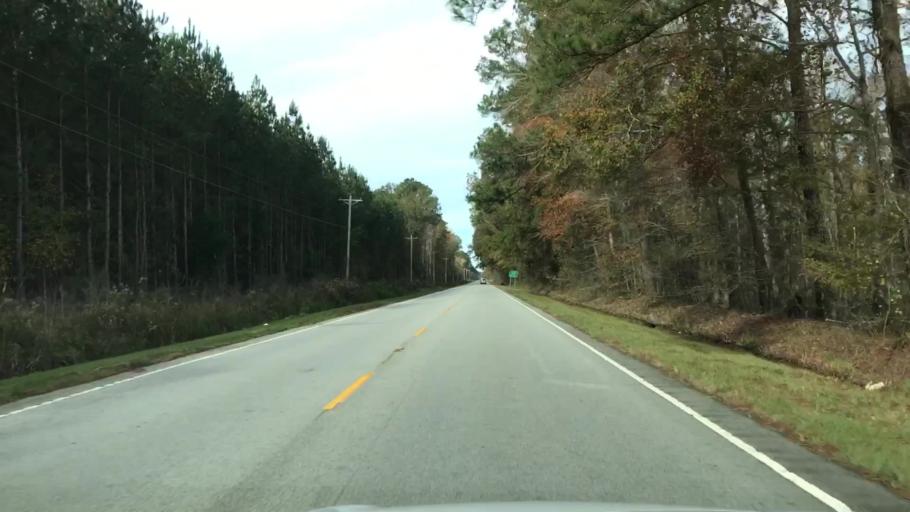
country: US
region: South Carolina
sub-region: Colleton County
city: Walterboro
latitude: 32.8090
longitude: -80.5226
